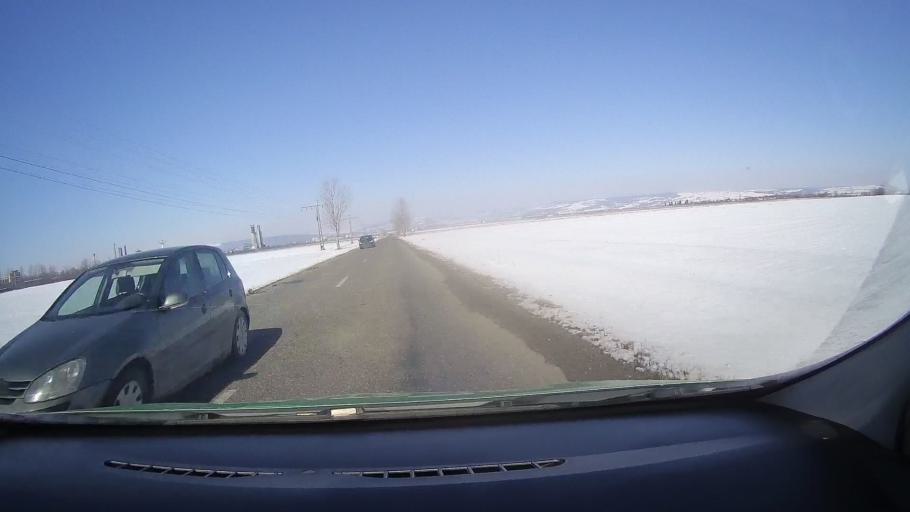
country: RO
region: Brasov
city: Fogarasch
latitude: 45.8010
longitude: 24.9928
